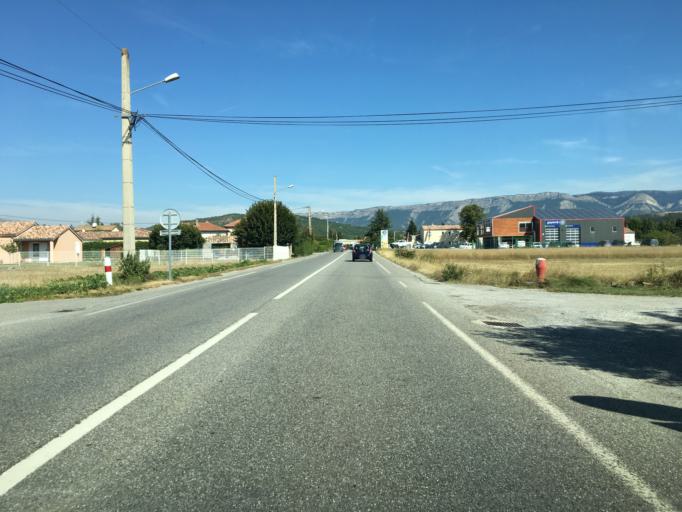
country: FR
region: Provence-Alpes-Cote d'Azur
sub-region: Departement des Hautes-Alpes
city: Laragne-Monteglin
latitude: 44.3052
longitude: 5.8362
